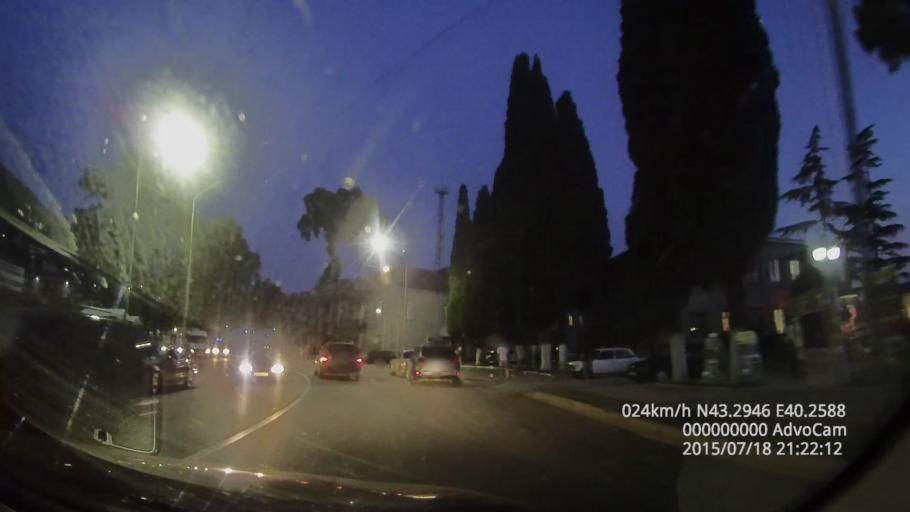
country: GE
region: Abkhazia
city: Gagra
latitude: 43.2945
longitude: 40.2589
